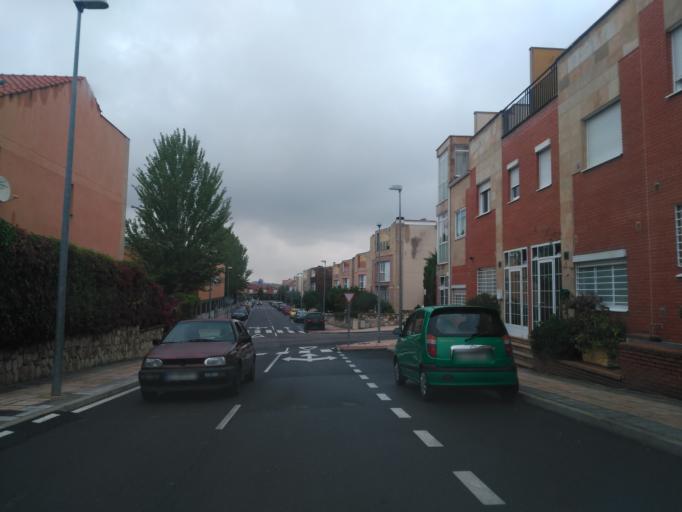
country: ES
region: Castille and Leon
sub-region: Provincia de Salamanca
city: Salamanca
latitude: 40.9508
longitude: -5.6814
